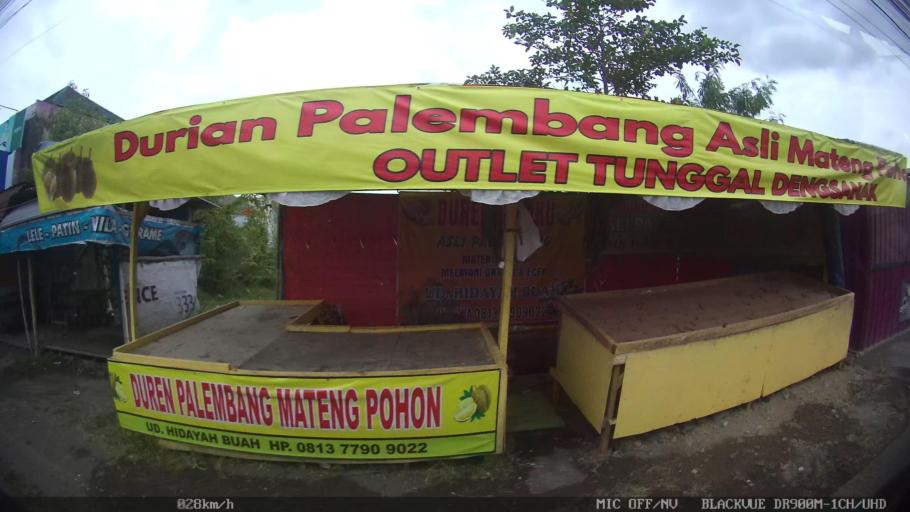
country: ID
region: Daerah Istimewa Yogyakarta
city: Sewon
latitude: -7.8415
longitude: 110.4112
